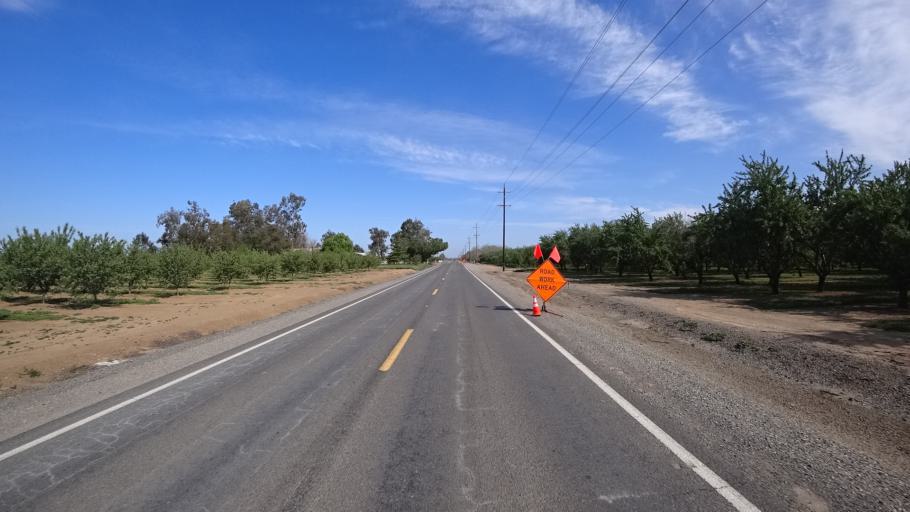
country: US
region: California
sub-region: Glenn County
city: Hamilton City
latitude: 39.6412
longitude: -122.0074
